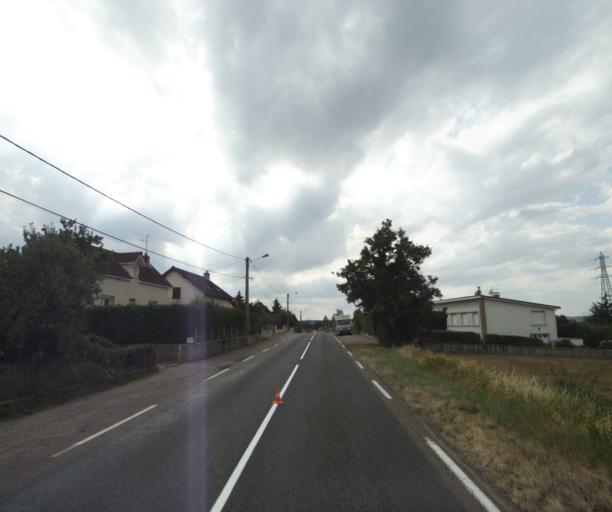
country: FR
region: Bourgogne
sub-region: Departement de Saone-et-Loire
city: Gueugnon
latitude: 46.6020
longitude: 4.0892
